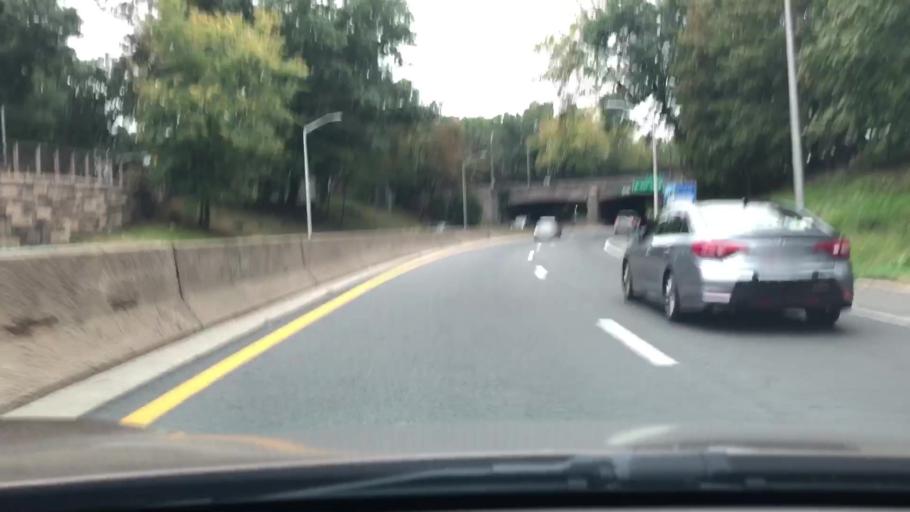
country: US
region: New York
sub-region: New York County
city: Inwood
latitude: 40.8903
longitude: -73.9083
